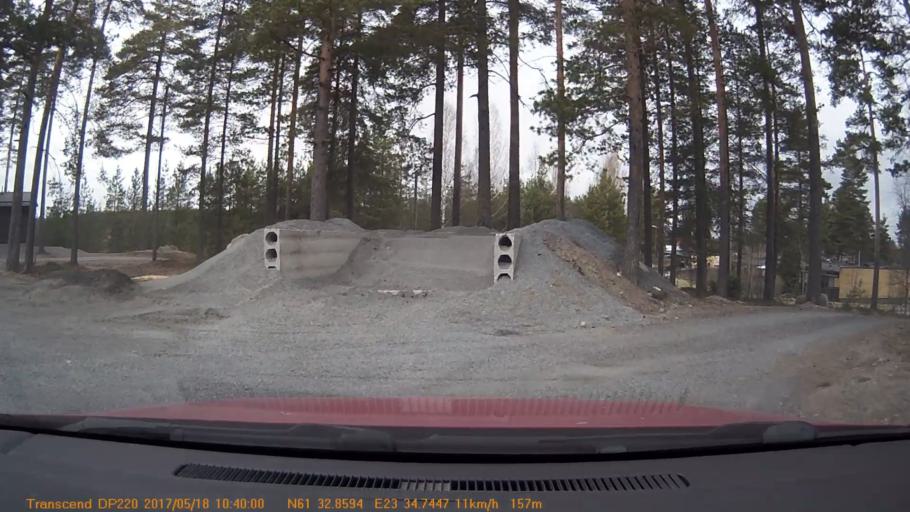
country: FI
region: Pirkanmaa
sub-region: Tampere
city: Yloejaervi
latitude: 61.5477
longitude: 23.5791
